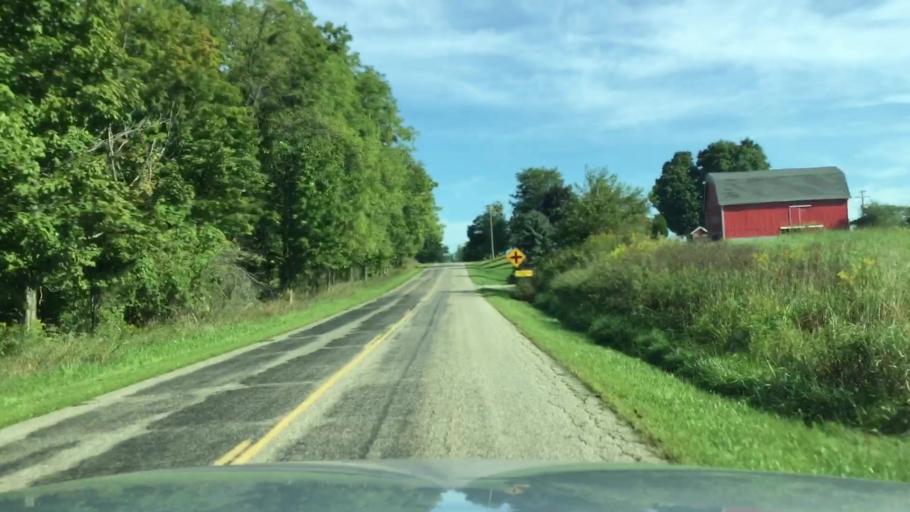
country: US
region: Michigan
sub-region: Lenawee County
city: Hudson
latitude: 41.9256
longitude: -84.4205
